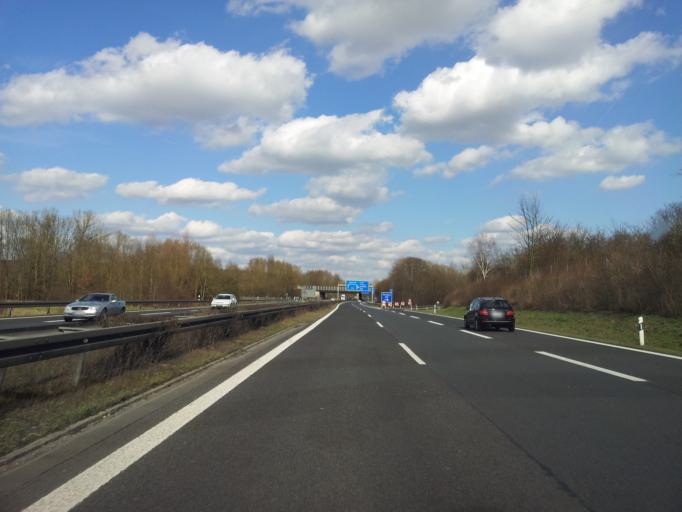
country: DE
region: Bavaria
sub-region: Upper Franconia
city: Gundelsheim
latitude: 49.9264
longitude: 10.9117
